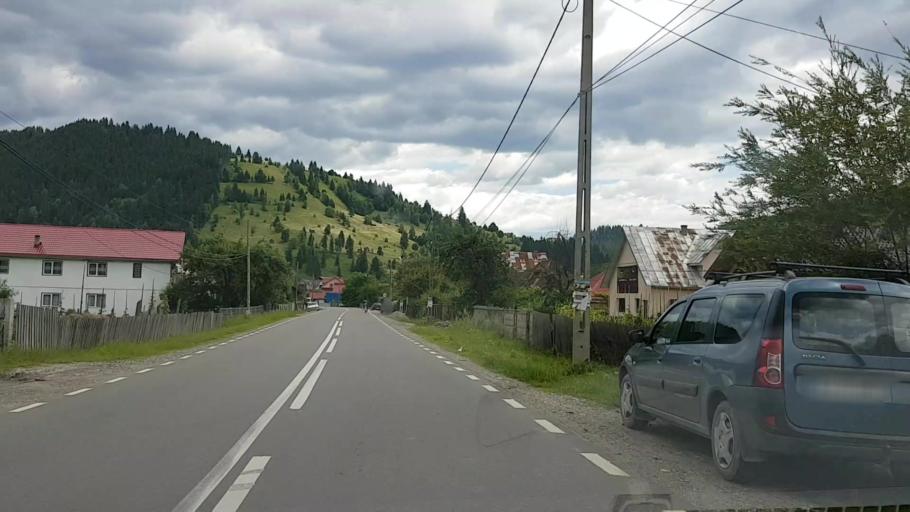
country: RO
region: Neamt
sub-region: Comuna Farcasa
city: Farcasa
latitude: 47.1577
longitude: 25.8327
